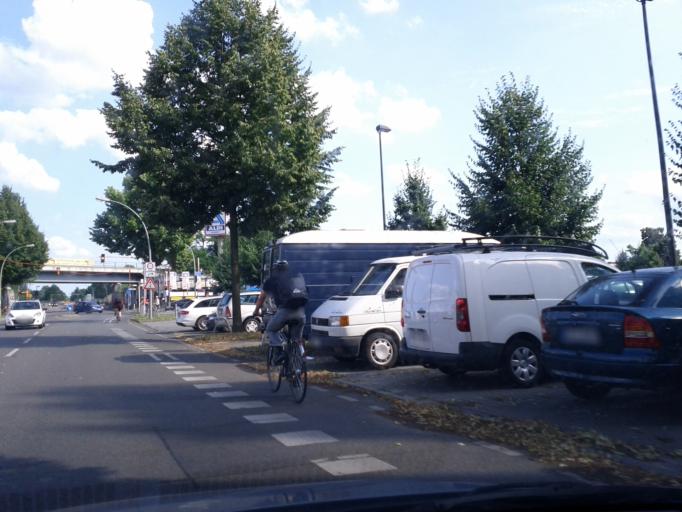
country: DE
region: Berlin
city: Treptow Bezirk
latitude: 52.4863
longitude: 13.4577
